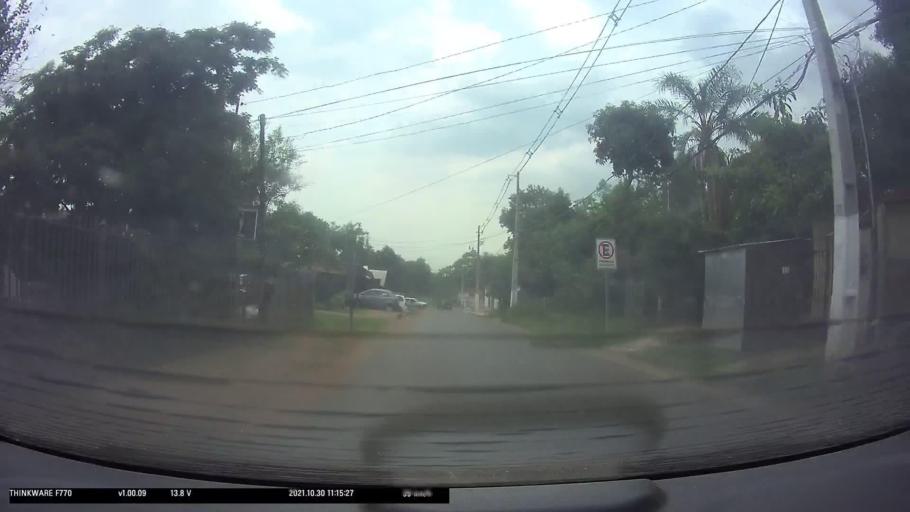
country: PY
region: Central
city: Fernando de la Mora
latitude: -25.3135
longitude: -57.5139
